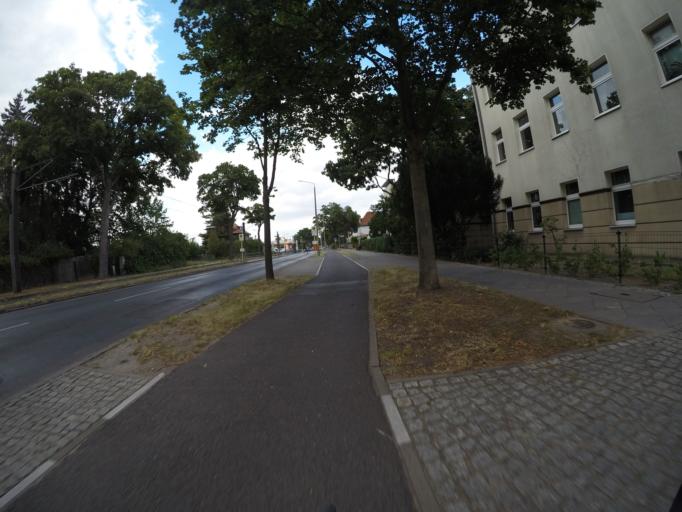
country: DE
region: Berlin
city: Mahlsdorf
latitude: 52.4850
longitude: 13.6034
